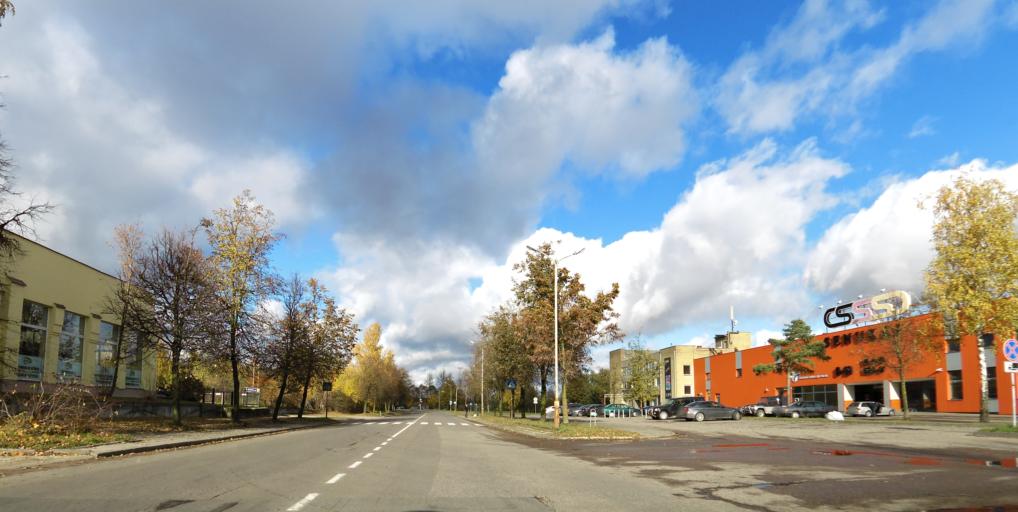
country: LT
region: Vilnius County
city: Vilkpede
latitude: 54.6441
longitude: 25.2660
